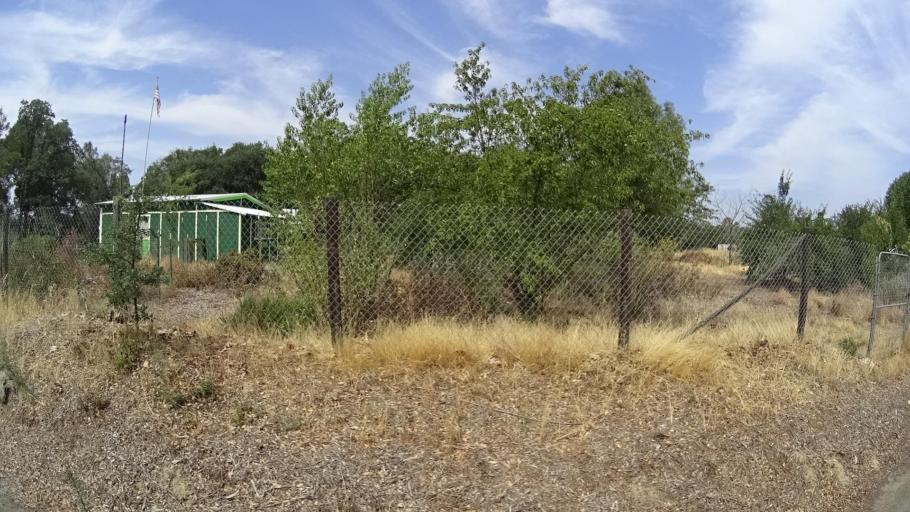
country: US
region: California
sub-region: Mariposa County
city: Mariposa
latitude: 37.4699
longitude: -119.8872
